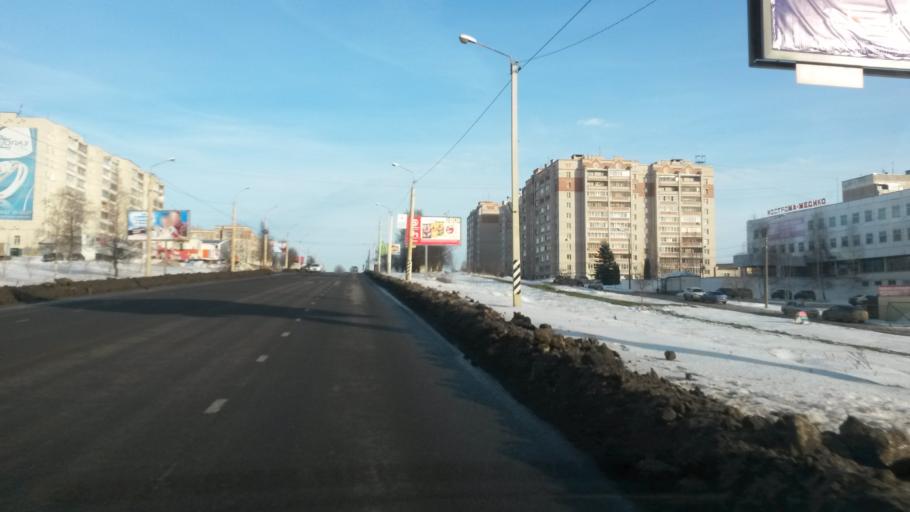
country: RU
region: Kostroma
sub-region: Kostromskoy Rayon
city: Kostroma
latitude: 57.7330
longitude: 40.9059
